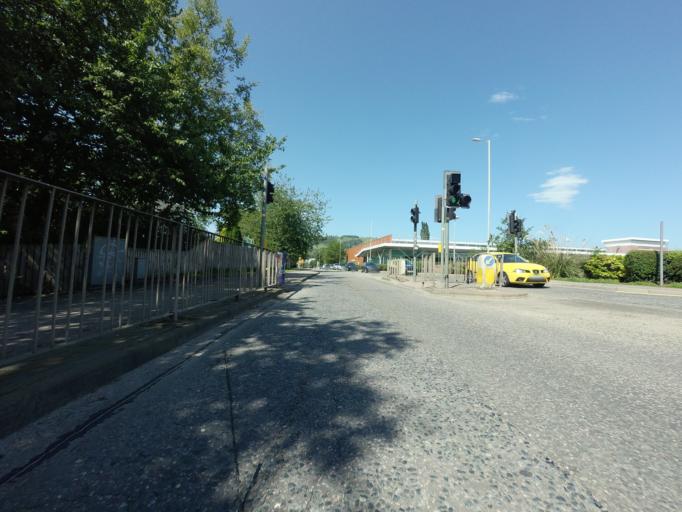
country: GB
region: Scotland
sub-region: Highland
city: Dingwall
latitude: 57.5968
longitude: -4.4316
